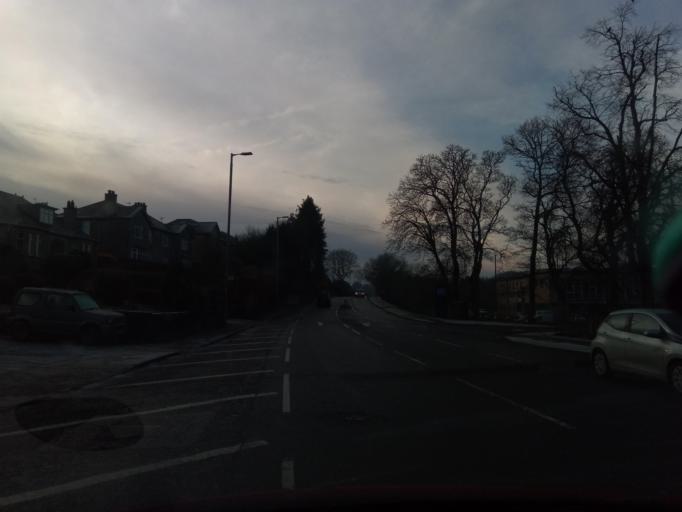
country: GB
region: Scotland
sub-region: The Scottish Borders
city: Hawick
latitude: 55.4323
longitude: -2.7808
